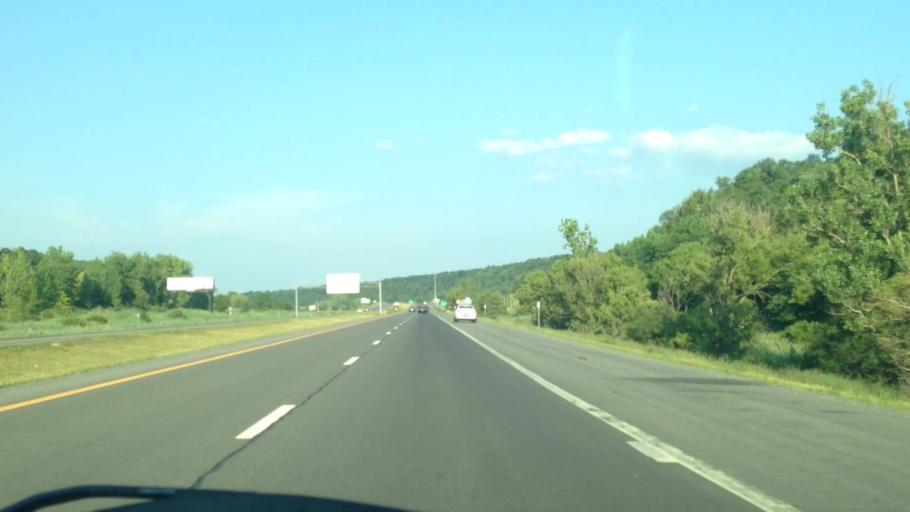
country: US
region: New York
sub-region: Onondaga County
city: Nedrow
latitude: 43.0054
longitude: -76.1131
